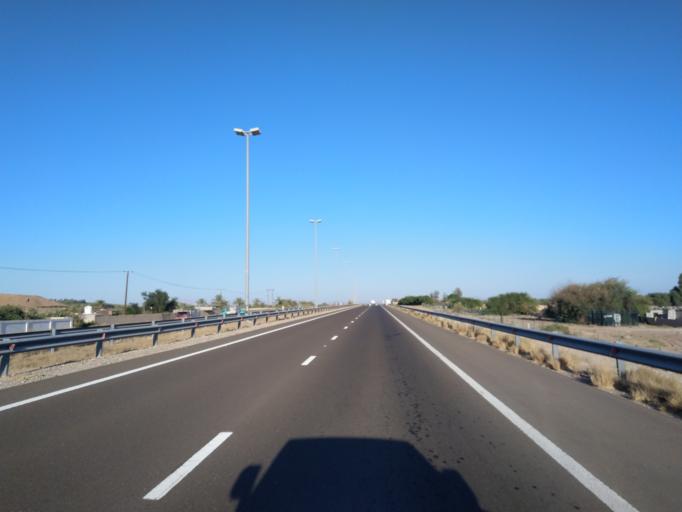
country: OM
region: Al Buraimi
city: Al Buraymi
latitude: 24.5464
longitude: 55.6629
